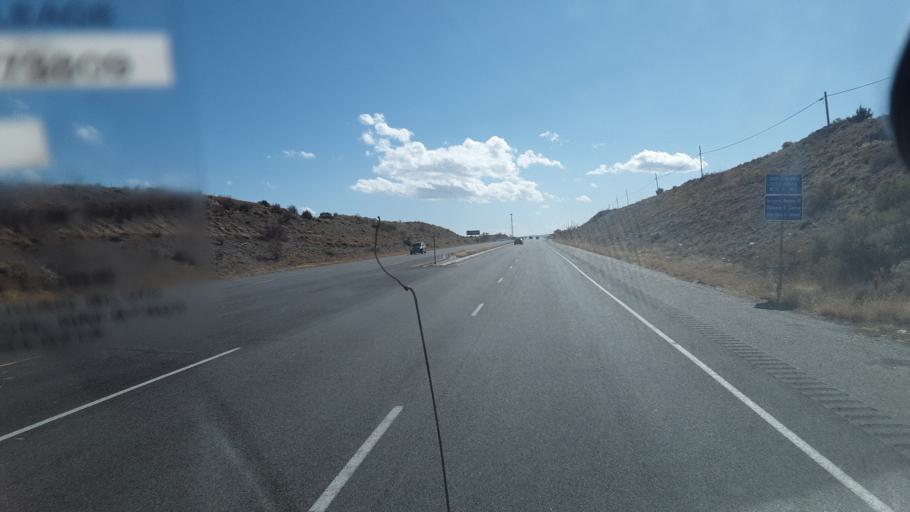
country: US
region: New Mexico
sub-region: Rio Arriba County
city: Ohkay Owingeh
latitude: 36.0277
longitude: -106.0929
